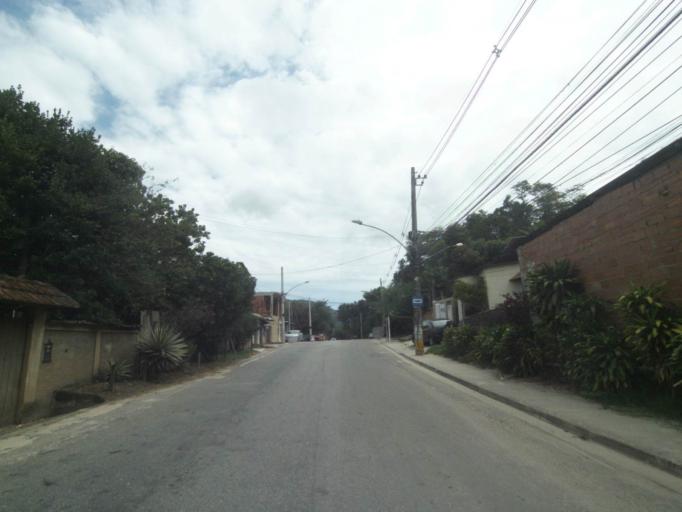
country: BR
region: Rio de Janeiro
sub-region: Nilopolis
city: Nilopolis
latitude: -23.0096
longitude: -43.5117
